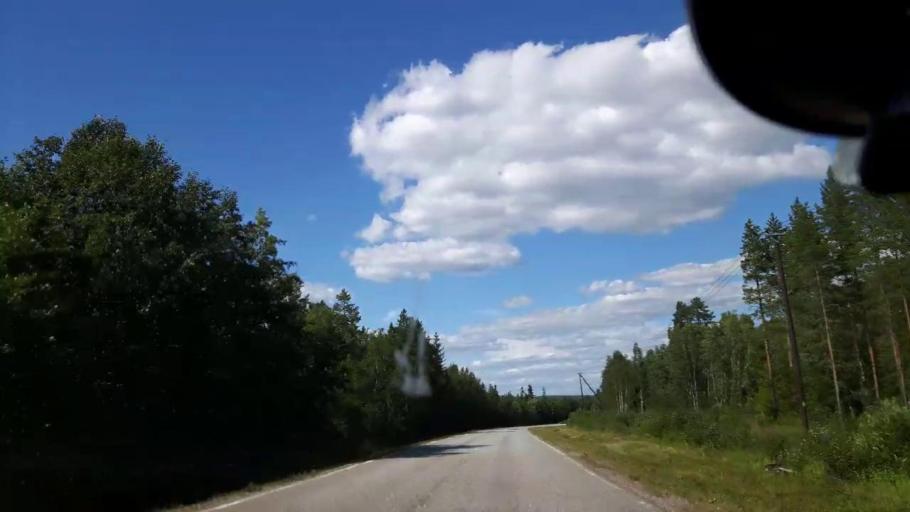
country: SE
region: Vaesternorrland
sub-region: Ange Kommun
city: Fransta
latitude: 62.7184
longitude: 16.3327
